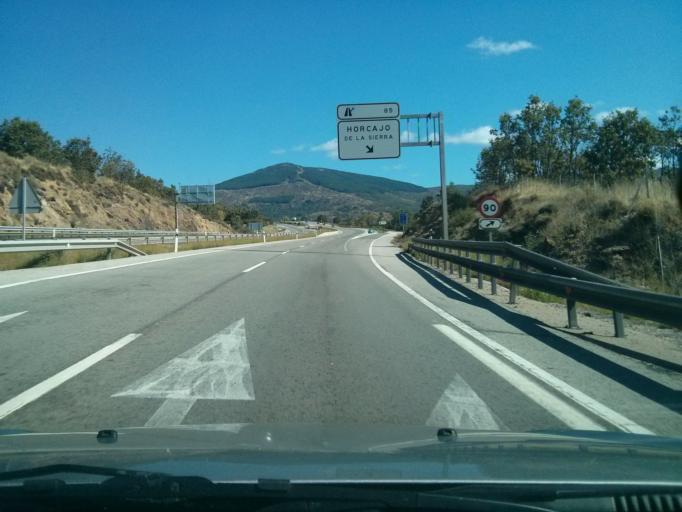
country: ES
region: Madrid
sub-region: Provincia de Madrid
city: Horcajo de la Sierra
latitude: 41.0776
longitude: -3.6026
